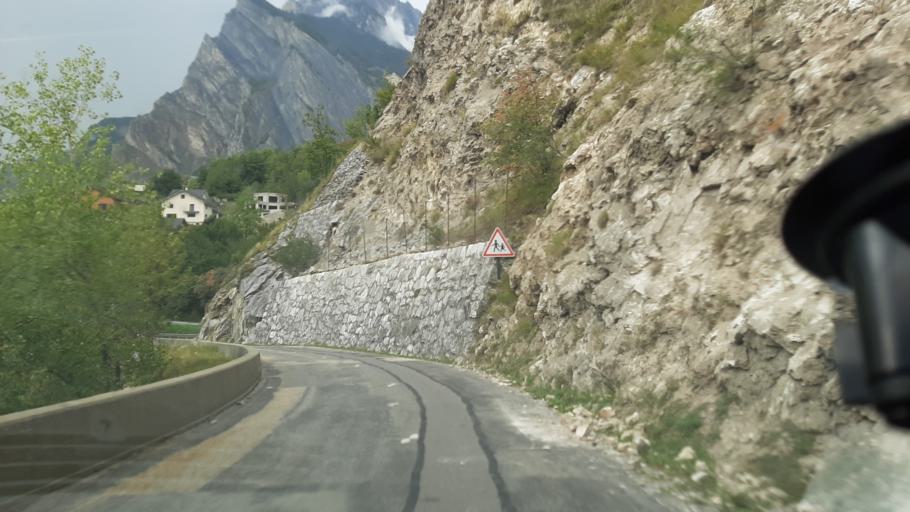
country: FR
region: Rhone-Alpes
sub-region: Departement de la Savoie
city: Saint-Michel-de-Maurienne
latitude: 45.2350
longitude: 6.4558
